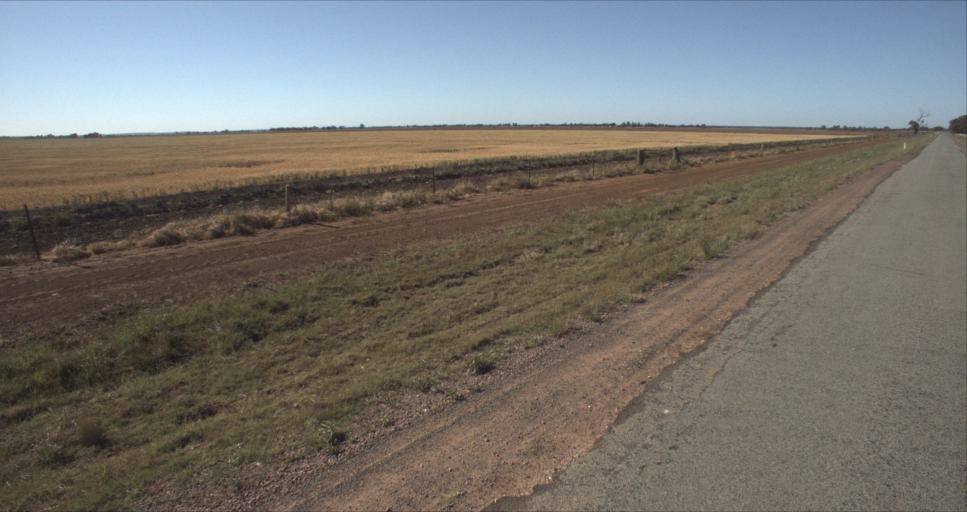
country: AU
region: New South Wales
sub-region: Leeton
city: Leeton
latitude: -34.5519
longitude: 146.3144
